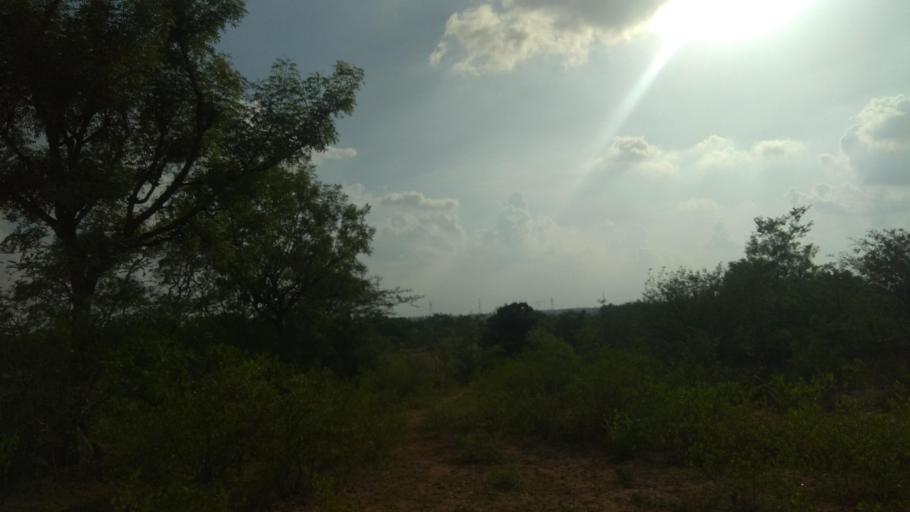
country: IN
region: Telangana
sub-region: Mahbubnagar
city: Farrukhnagar
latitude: 16.8886
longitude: 78.4784
